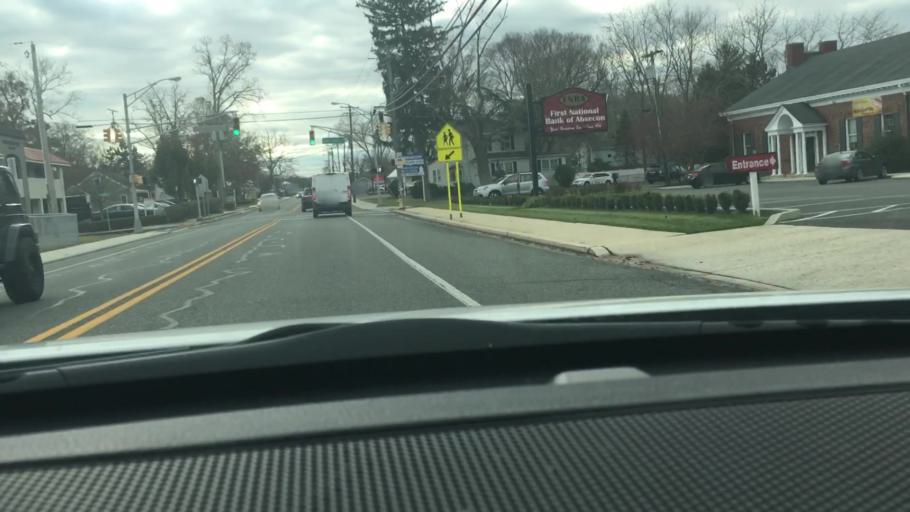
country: US
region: New Jersey
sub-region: Atlantic County
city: Northfield
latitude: 39.3668
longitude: -74.5623
